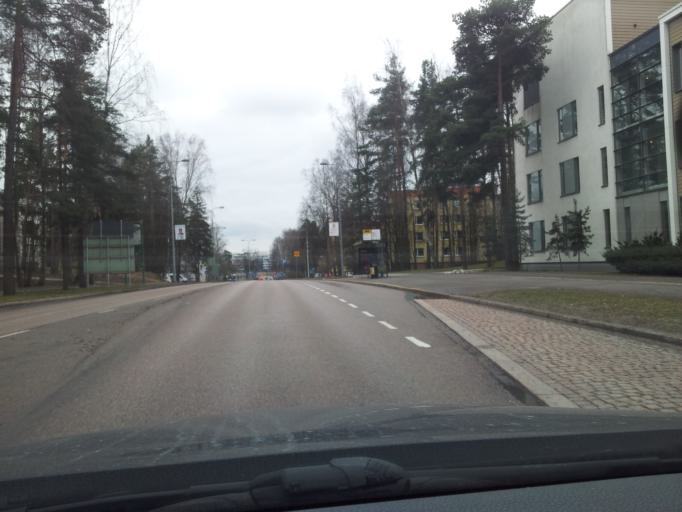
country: FI
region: Uusimaa
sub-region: Helsinki
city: Otaniemi
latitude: 60.1785
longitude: 24.7987
